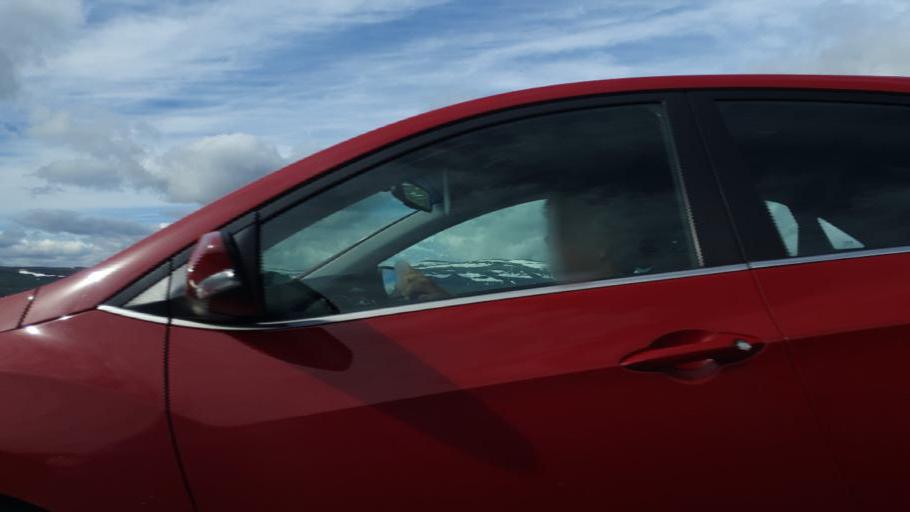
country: NO
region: Oppland
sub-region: Vestre Slidre
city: Slidre
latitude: 61.2736
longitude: 8.8570
